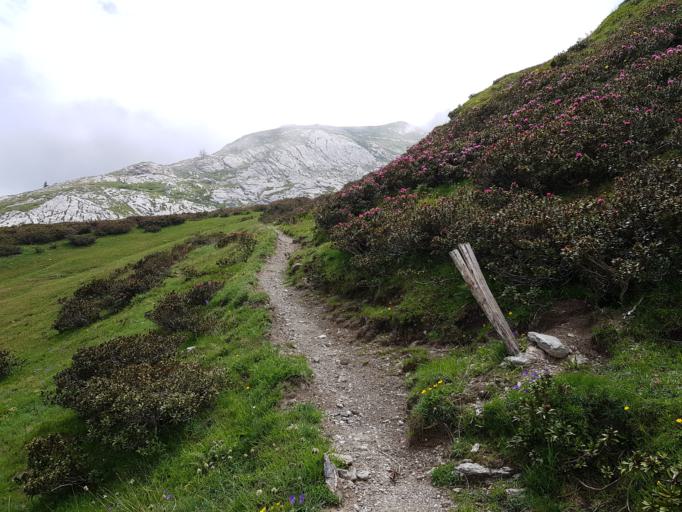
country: IT
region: Piedmont
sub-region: Provincia di Cuneo
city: Frabosa Soprana
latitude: 44.1922
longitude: 7.7717
